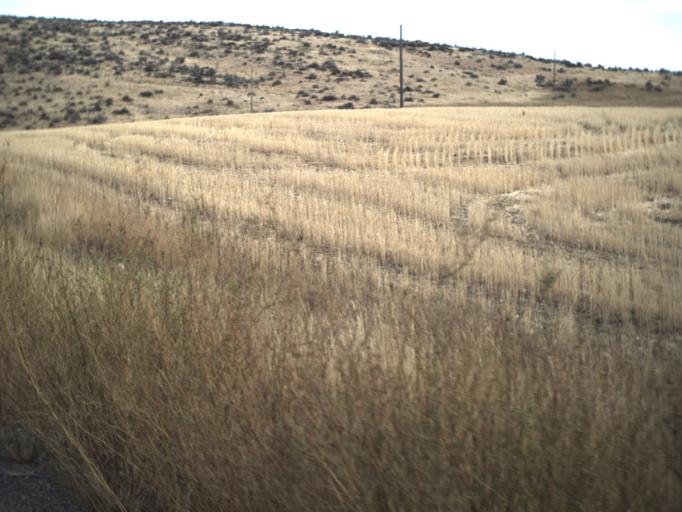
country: US
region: Utah
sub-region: Box Elder County
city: Garland
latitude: 41.8984
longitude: -112.5442
